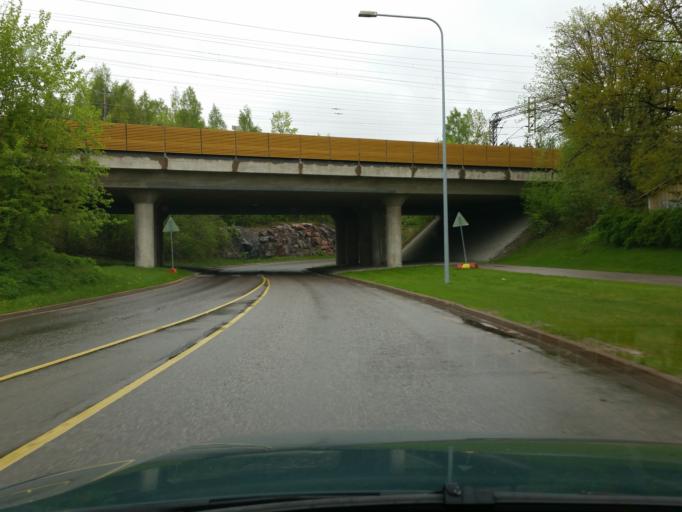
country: FI
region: Uusimaa
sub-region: Helsinki
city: Teekkarikylae
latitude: 60.2184
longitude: 24.8358
